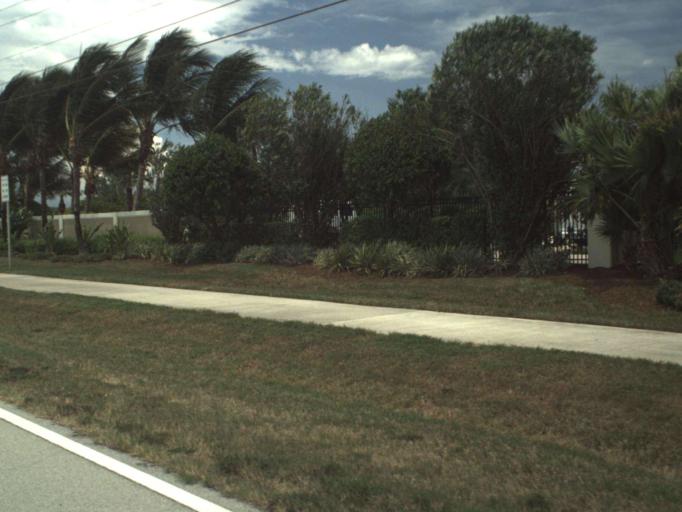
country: US
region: Florida
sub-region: Saint Lucie County
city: Hutchinson Island South
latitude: 27.3136
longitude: -80.2240
